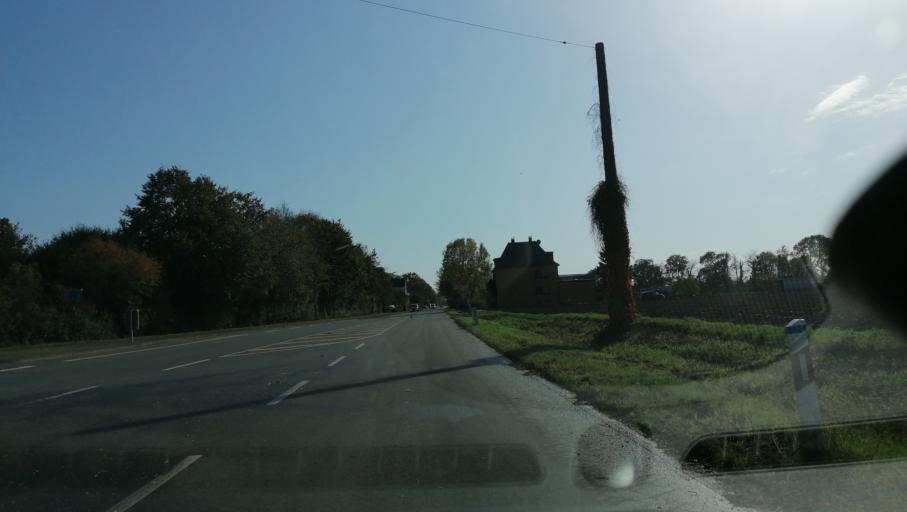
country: DE
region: North Rhine-Westphalia
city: Waltrop
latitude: 51.6162
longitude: 7.4349
